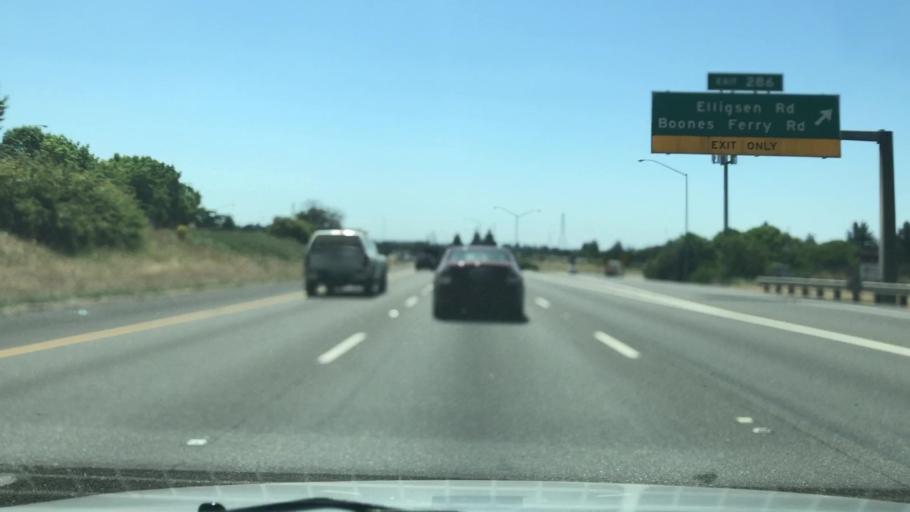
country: US
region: Oregon
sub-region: Clackamas County
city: Wilsonville
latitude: 45.3401
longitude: -122.7693
